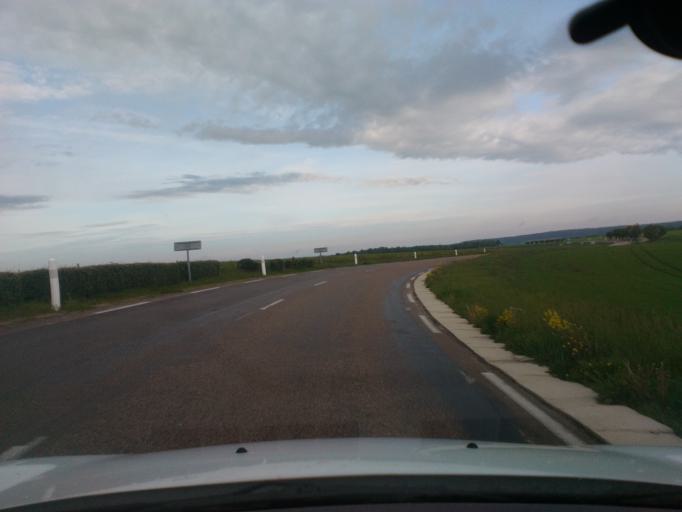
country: FR
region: Champagne-Ardenne
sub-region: Departement de la Haute-Marne
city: Lavilleneuve-au-Roi
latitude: 48.2261
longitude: 4.8761
